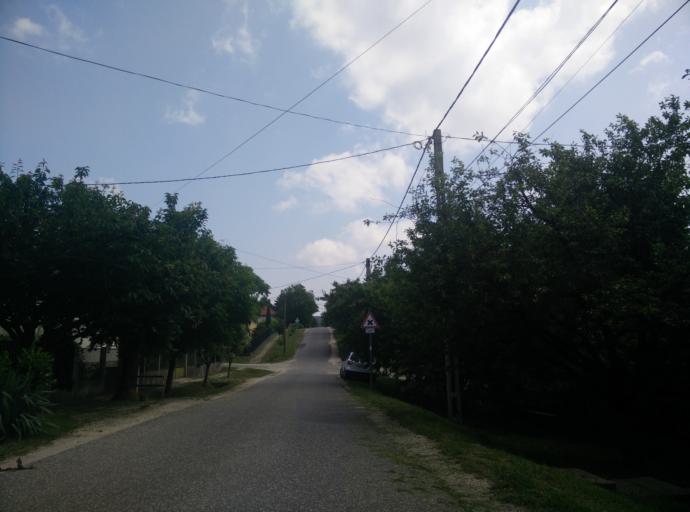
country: HU
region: Pest
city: Biatorbagy
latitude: 47.4652
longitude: 18.8156
